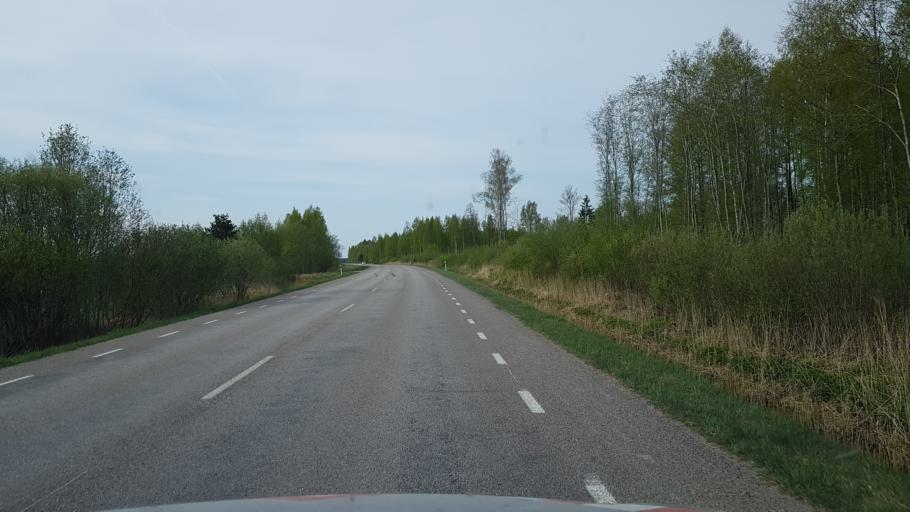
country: EE
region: Paernumaa
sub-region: Audru vald
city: Audru
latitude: 58.3879
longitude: 24.2740
